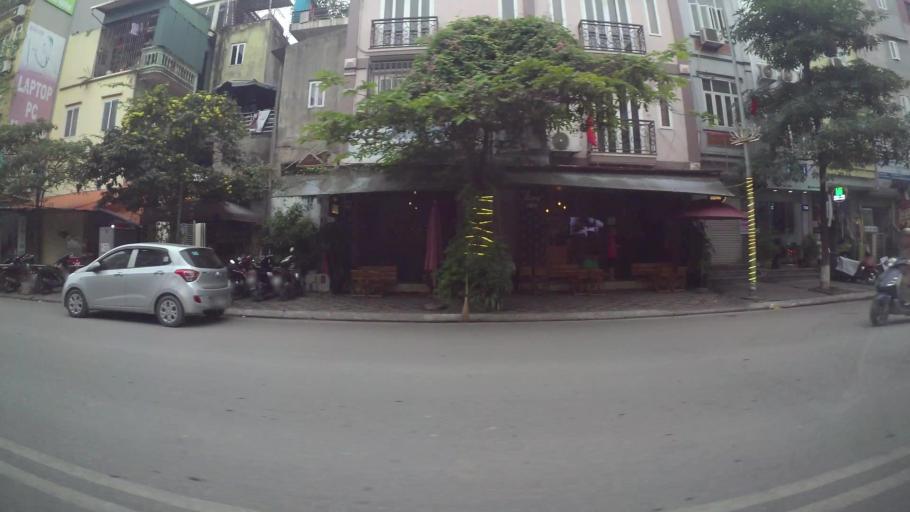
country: VN
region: Ha Noi
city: Hai BaTrung
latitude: 21.0031
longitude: 105.8521
